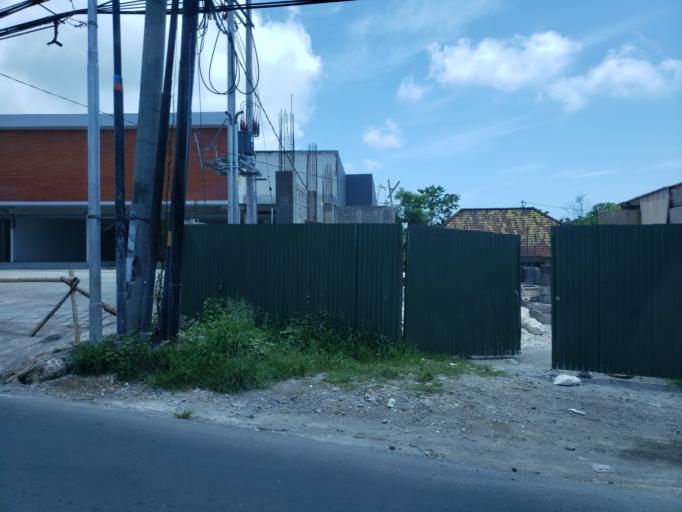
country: ID
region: Bali
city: Kangin
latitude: -8.8269
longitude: 115.1398
